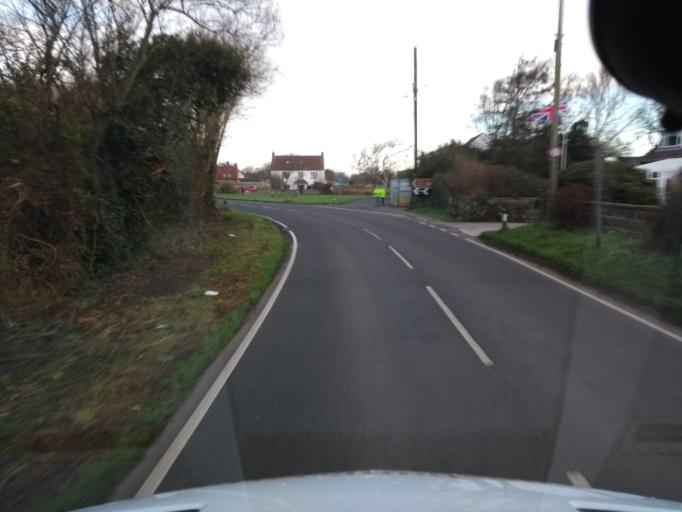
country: GB
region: England
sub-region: Somerset
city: Burnham-on-Sea
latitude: 51.2739
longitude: -3.0120
